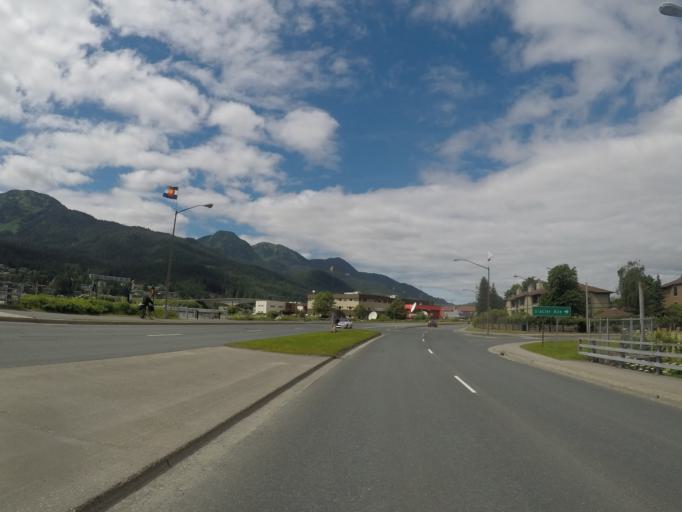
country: US
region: Alaska
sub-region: Juneau City and Borough
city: Juneau
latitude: 58.2991
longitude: -134.4199
